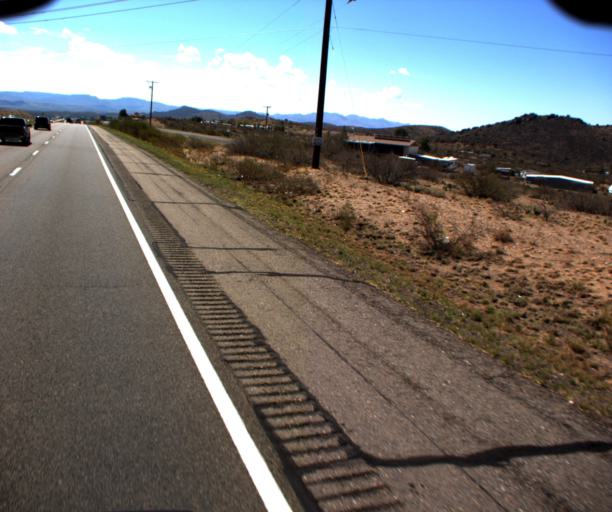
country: US
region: Arizona
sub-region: Yavapai County
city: Spring Valley
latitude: 34.3412
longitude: -112.1370
